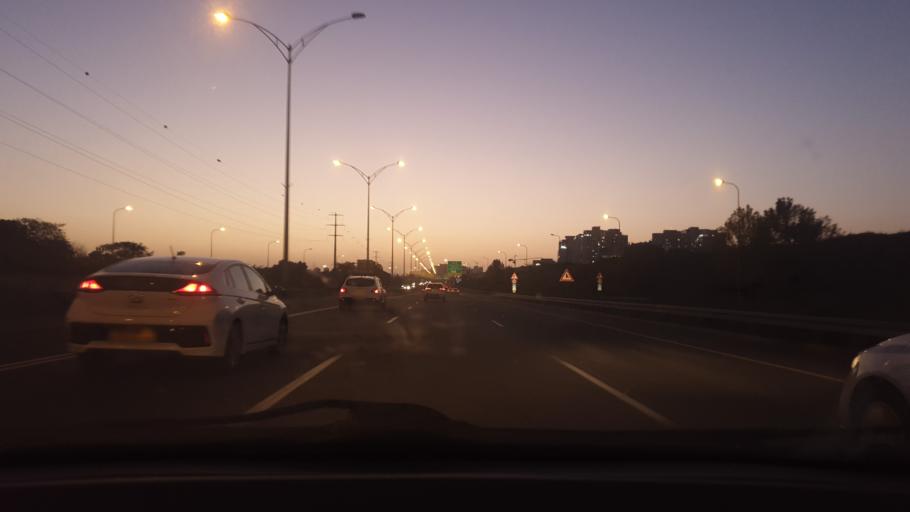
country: IL
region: Central District
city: Nehalim
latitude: 32.0677
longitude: 34.9182
